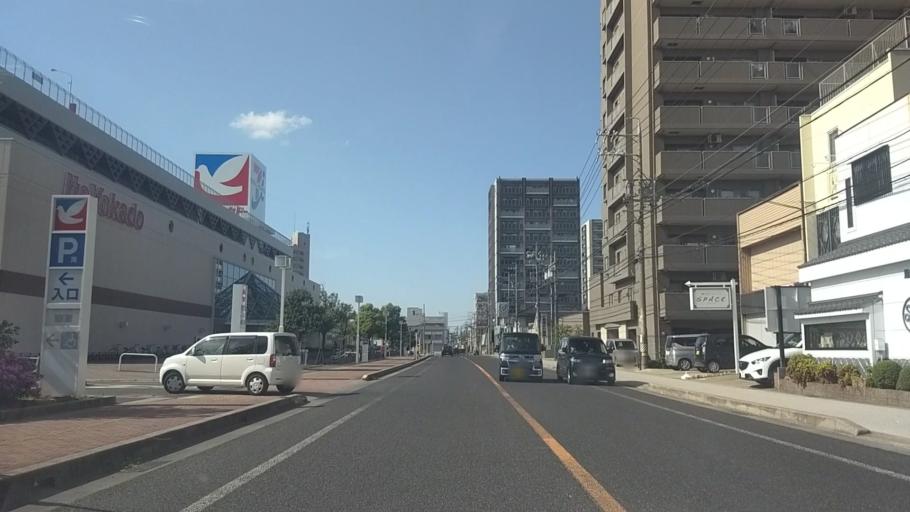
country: JP
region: Aichi
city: Anjo
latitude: 34.9843
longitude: 137.0843
